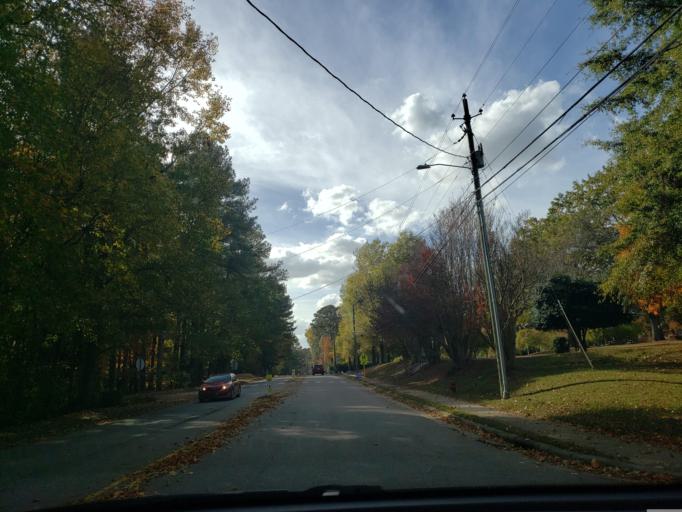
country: US
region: North Carolina
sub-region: Wake County
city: Apex
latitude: 35.7361
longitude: -78.8534
